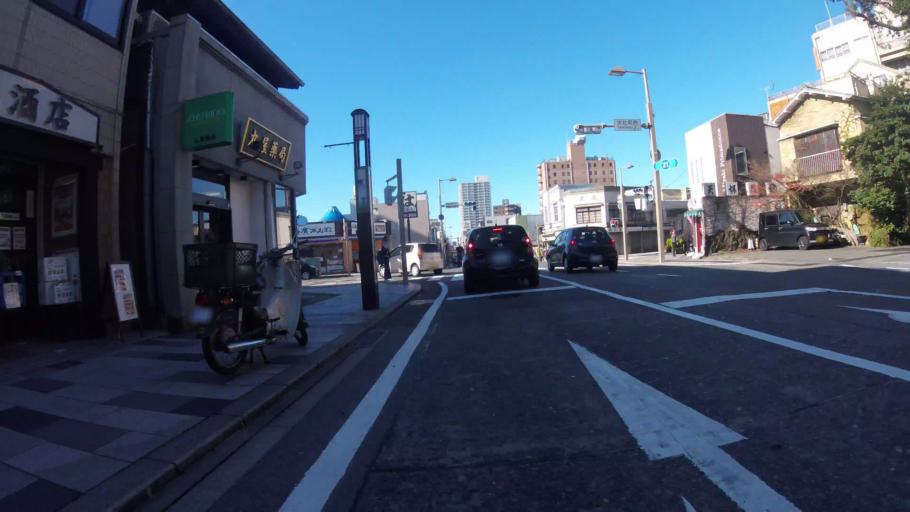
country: JP
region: Shizuoka
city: Mishima
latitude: 35.1201
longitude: 138.9190
